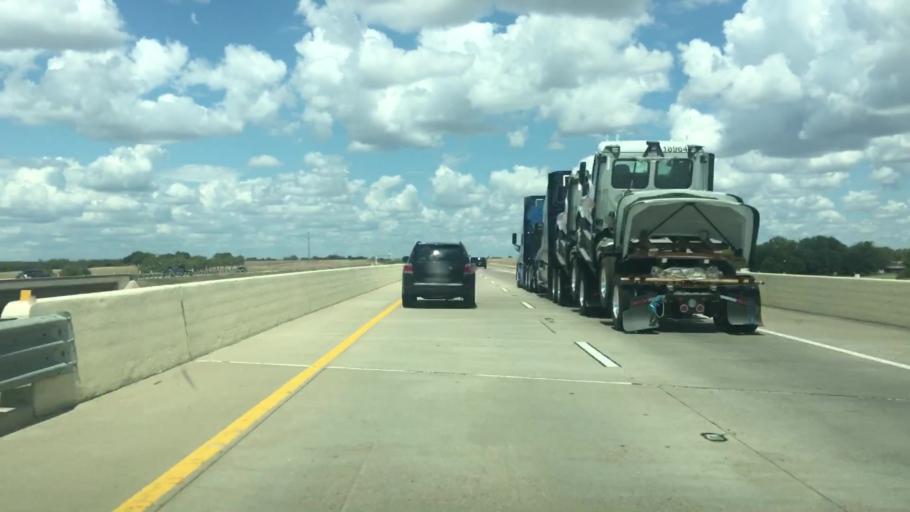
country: US
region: Texas
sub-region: Williamson County
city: Hutto
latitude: 30.5619
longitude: -97.5788
